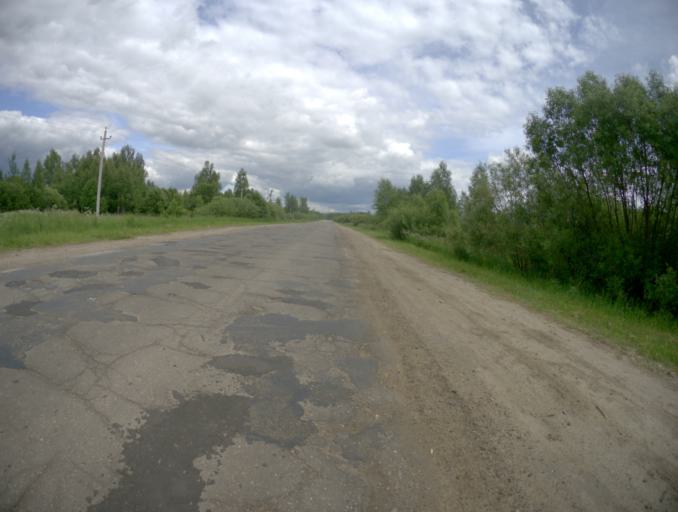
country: RU
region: Ivanovo
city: Savino
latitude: 56.6072
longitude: 41.2345
